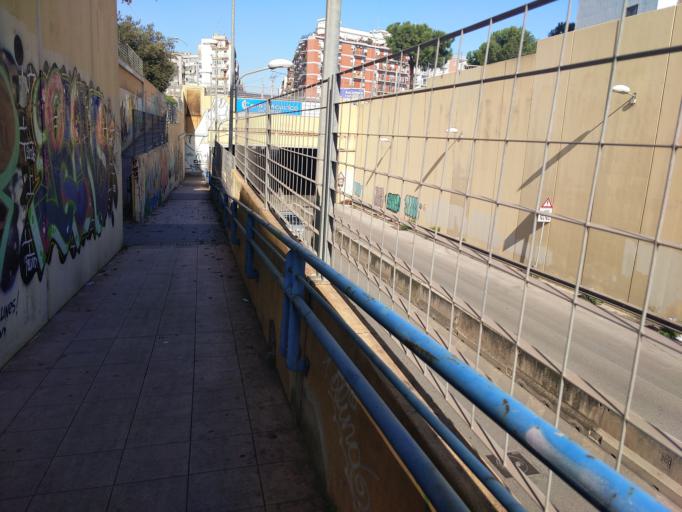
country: IT
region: Apulia
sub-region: Provincia di Bari
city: Bari
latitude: 41.1166
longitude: 16.8525
